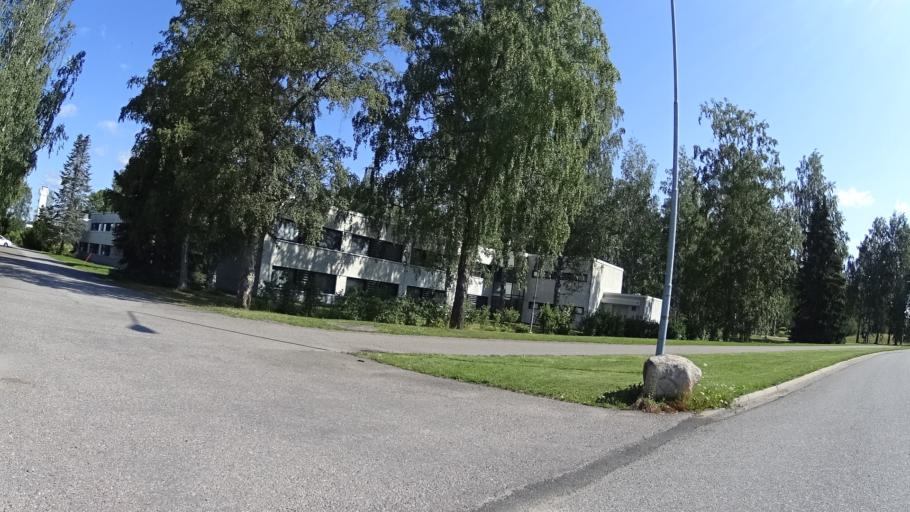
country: FI
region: Uusimaa
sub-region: Helsinki
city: Tuusula
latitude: 60.4120
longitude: 25.0373
